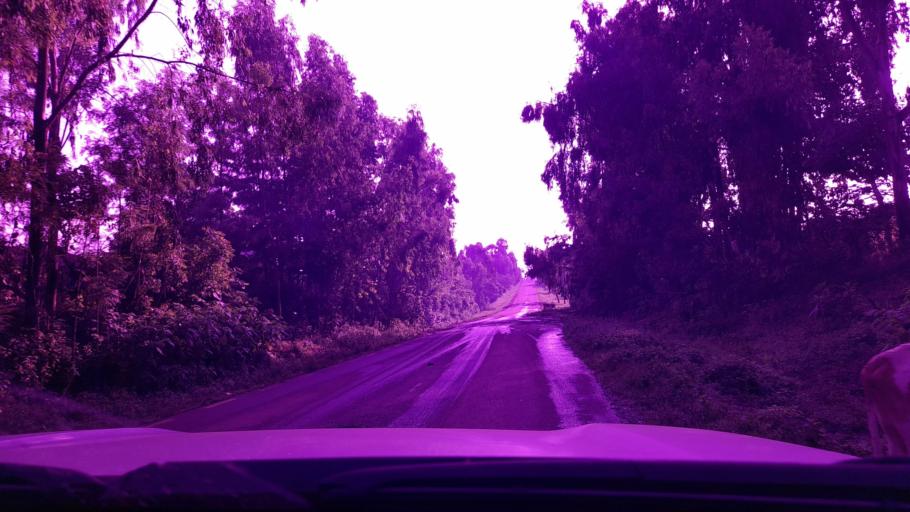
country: ET
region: Oromiya
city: Bedele
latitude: 8.1515
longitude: 36.4667
